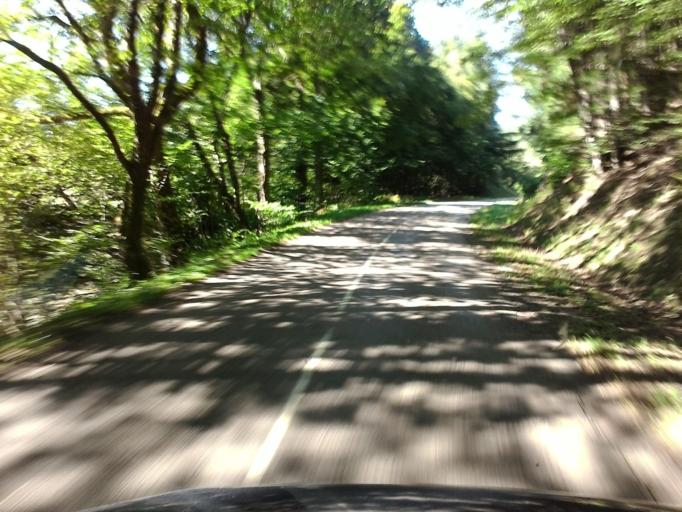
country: FR
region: Bourgogne
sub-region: Departement de la Nievre
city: Lormes
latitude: 47.2682
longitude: 3.8484
